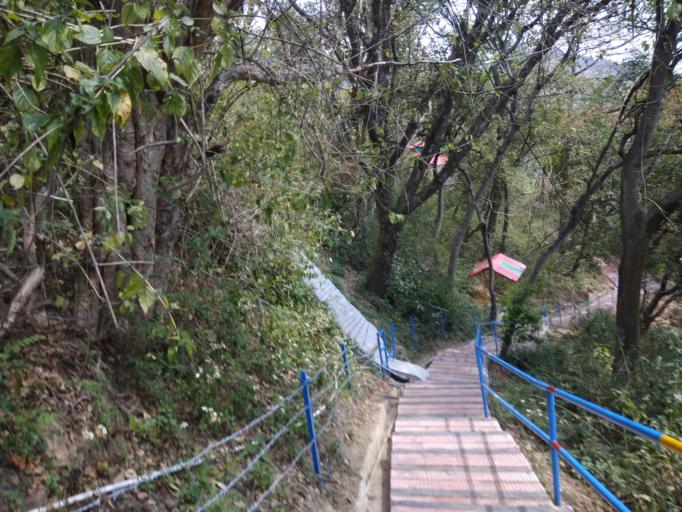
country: IN
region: Himachal Pradesh
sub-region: Kangra
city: Palampur
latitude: 32.0764
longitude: 76.6240
